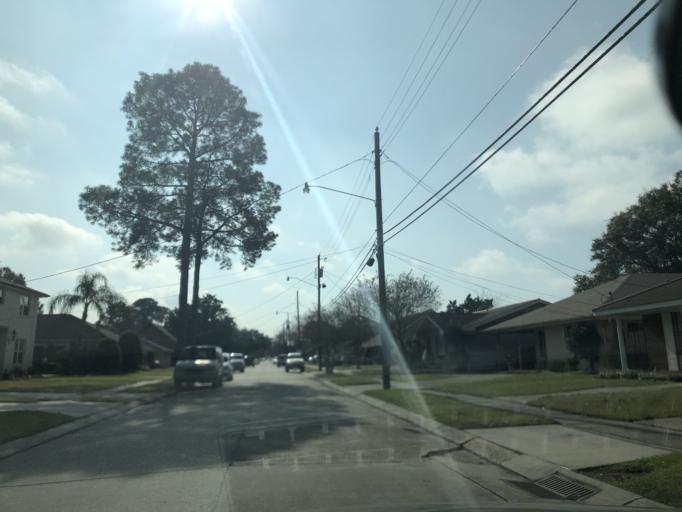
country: US
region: Louisiana
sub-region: Jefferson Parish
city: Metairie
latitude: 29.9947
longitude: -90.1484
